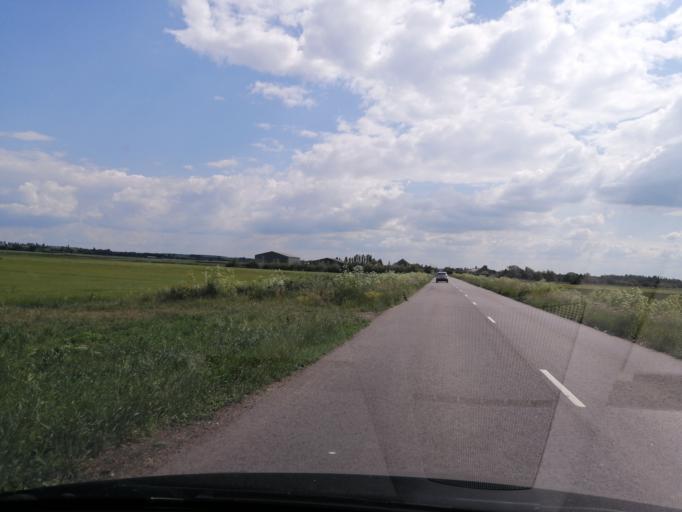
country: GB
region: England
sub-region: Cambridgeshire
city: Ramsey
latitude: 52.4618
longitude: -0.1556
